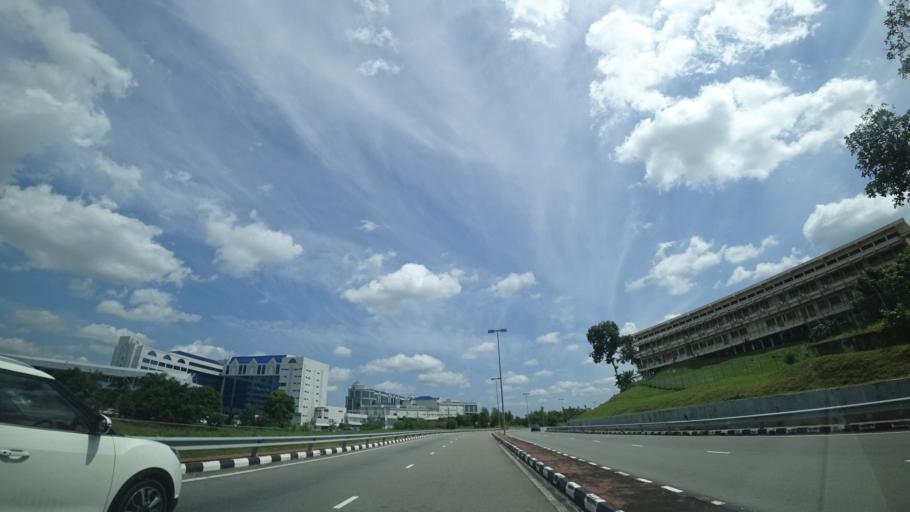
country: BN
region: Brunei and Muara
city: Bandar Seri Begawan
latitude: 4.9073
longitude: 114.9134
